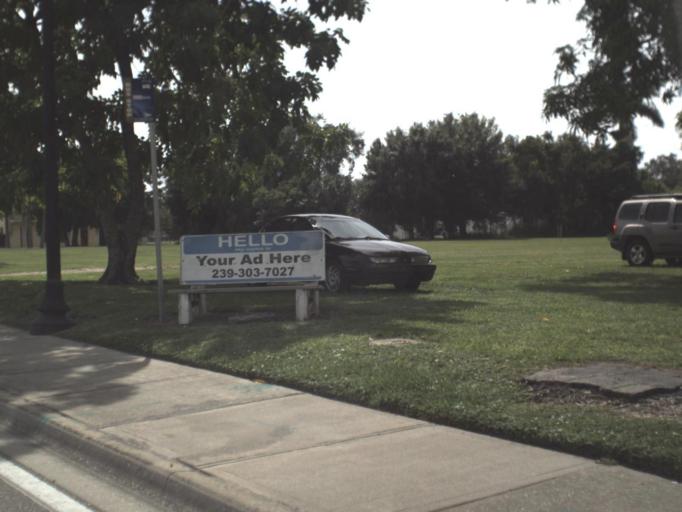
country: US
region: Florida
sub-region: Lee County
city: North Fort Myers
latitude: 26.6455
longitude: -81.8654
